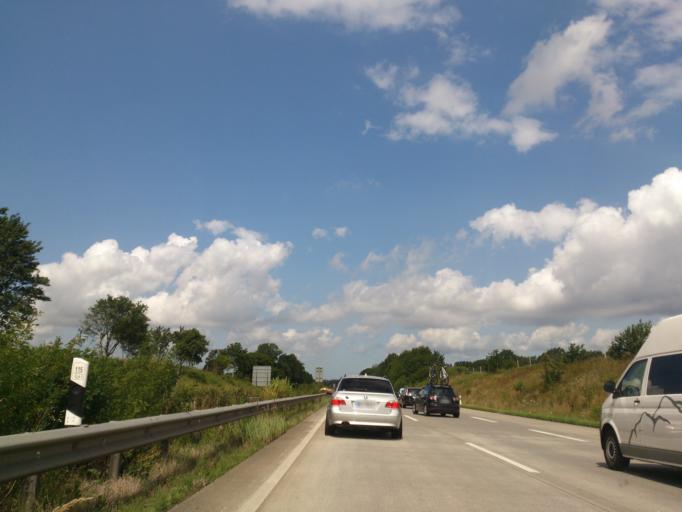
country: DE
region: Schleswig-Holstein
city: Neuenbrook
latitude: 53.8753
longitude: 9.5560
